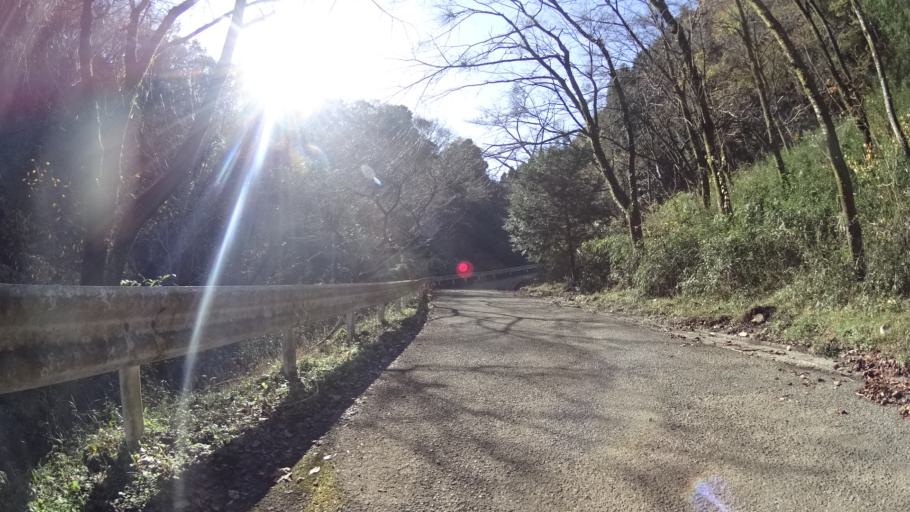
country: JP
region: Kanagawa
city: Atsugi
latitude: 35.5138
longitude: 139.2719
